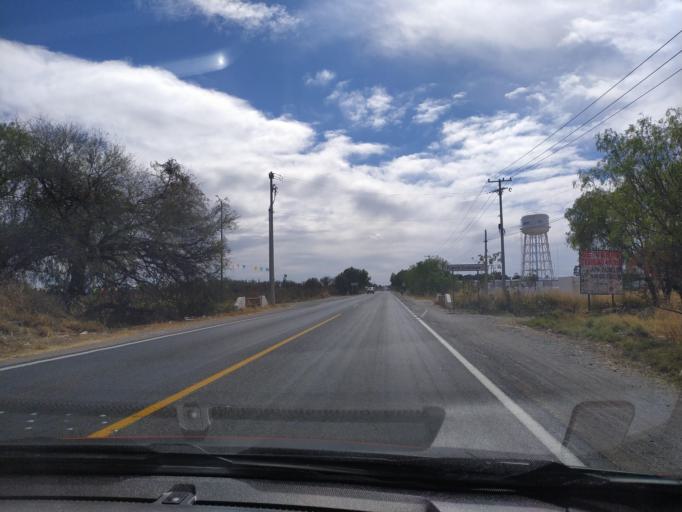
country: LA
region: Oudomxai
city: Muang La
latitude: 21.0247
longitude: 101.8256
